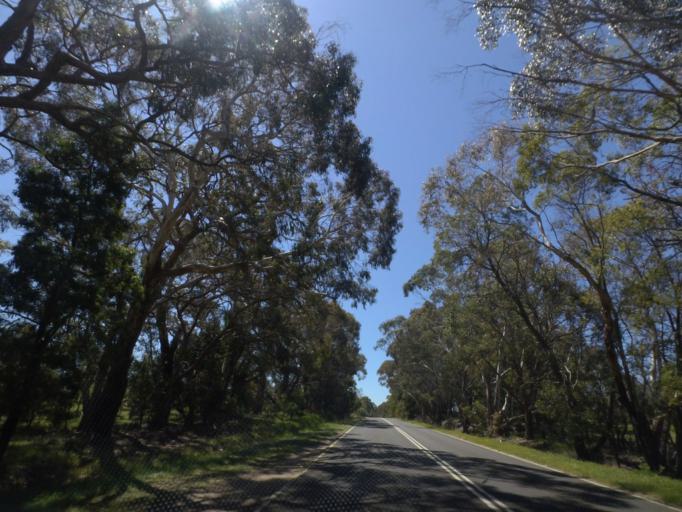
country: AU
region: Victoria
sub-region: Hume
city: Sunbury
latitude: -37.2072
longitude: 144.7420
